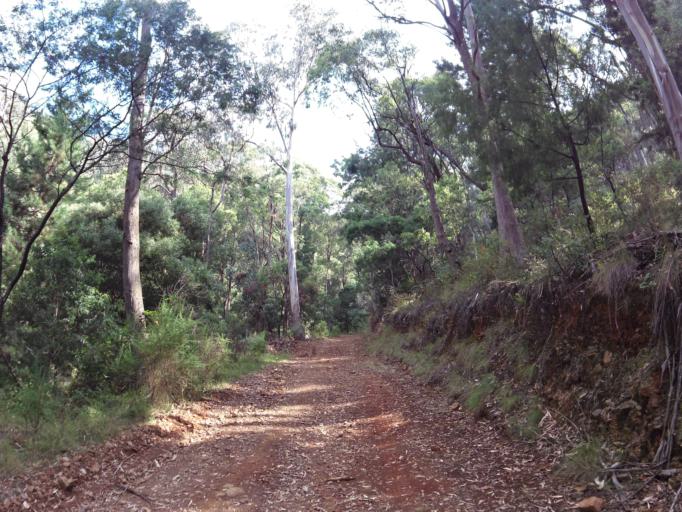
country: AU
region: Victoria
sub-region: Alpine
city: Mount Beauty
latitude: -36.7745
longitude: 147.0135
